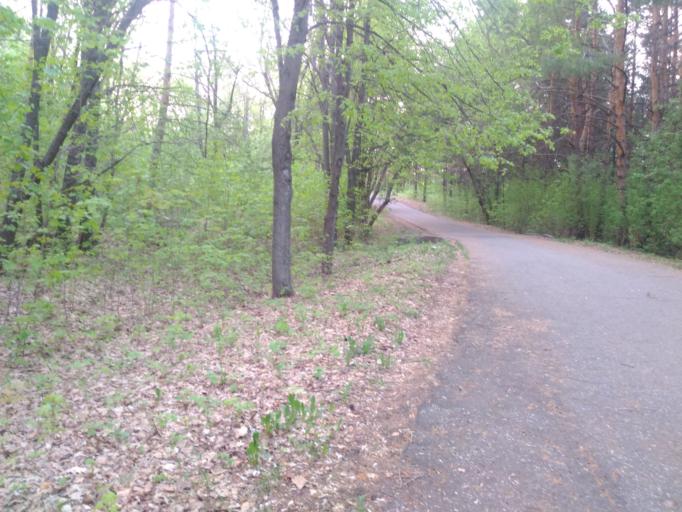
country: RU
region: Ulyanovsk
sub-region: Ulyanovskiy Rayon
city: Ulyanovsk
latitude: 54.2740
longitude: 48.3571
